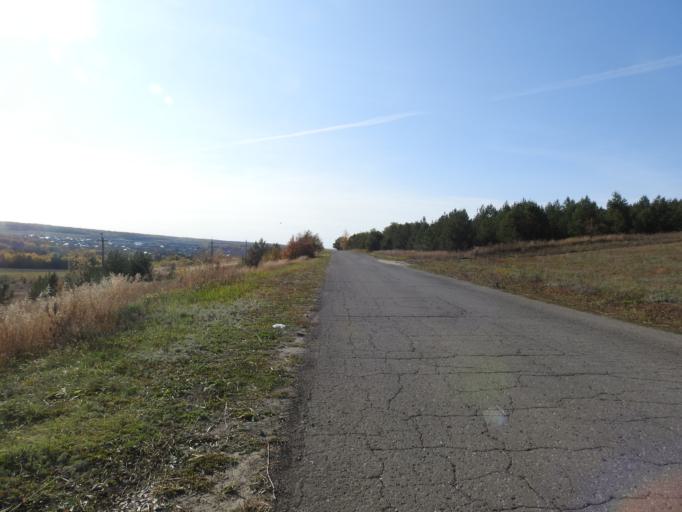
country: RU
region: Saratov
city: Baltay
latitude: 52.4681
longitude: 46.6590
